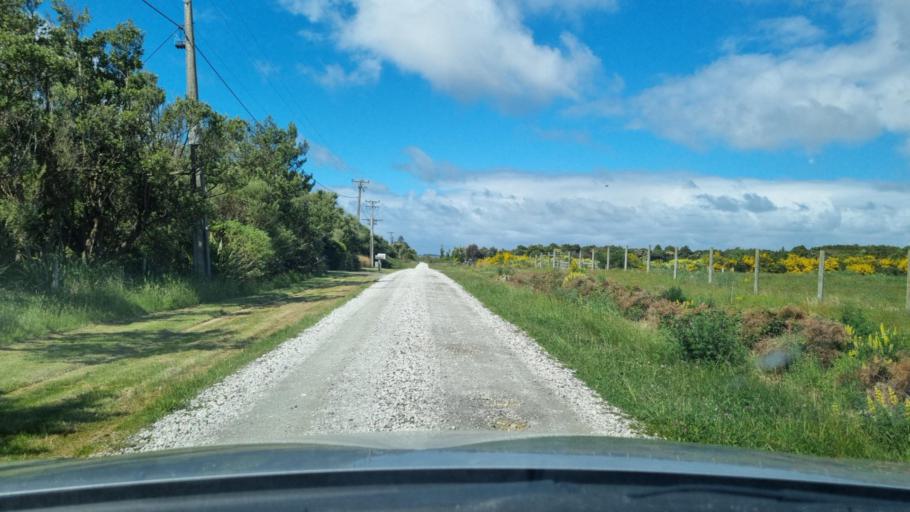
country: NZ
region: Southland
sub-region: Invercargill City
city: Invercargill
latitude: -46.4499
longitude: 168.3166
